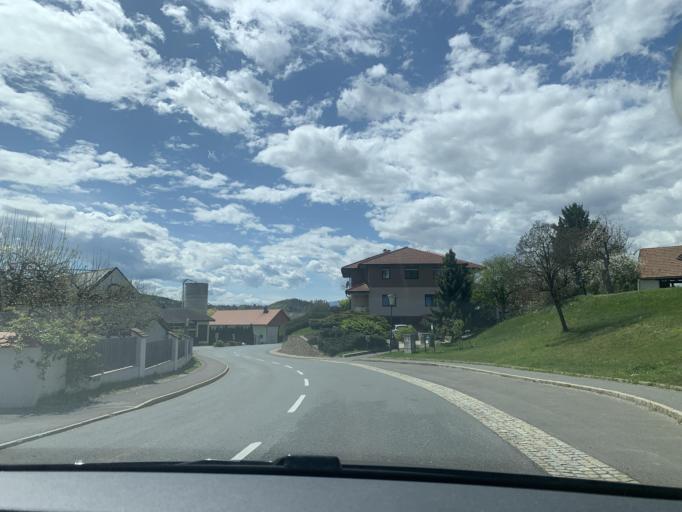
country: AT
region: Styria
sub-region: Politischer Bezirk Leibnitz
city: Weitendorf
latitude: 46.8973
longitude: 15.4661
